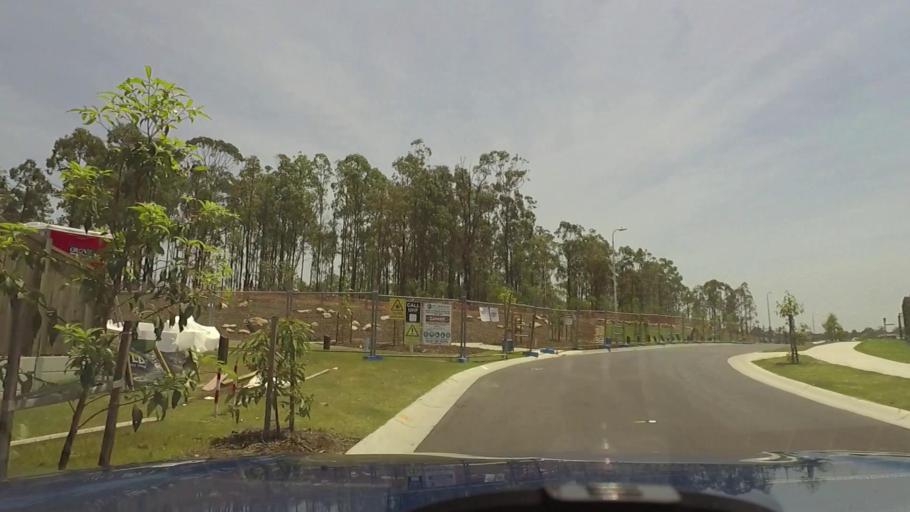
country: AU
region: Queensland
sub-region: Logan
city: Chambers Flat
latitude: -27.8086
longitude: 153.1240
